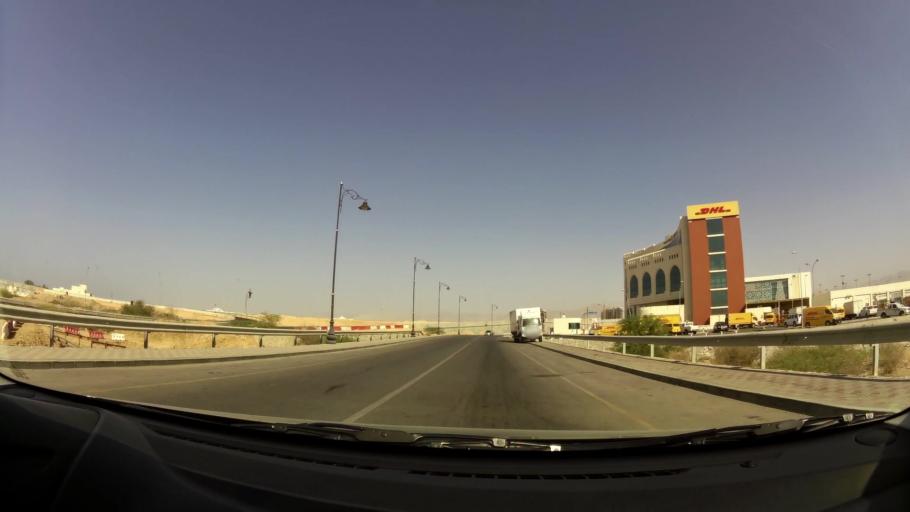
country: OM
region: Muhafazat Masqat
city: Bawshar
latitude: 23.5813
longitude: 58.2920
